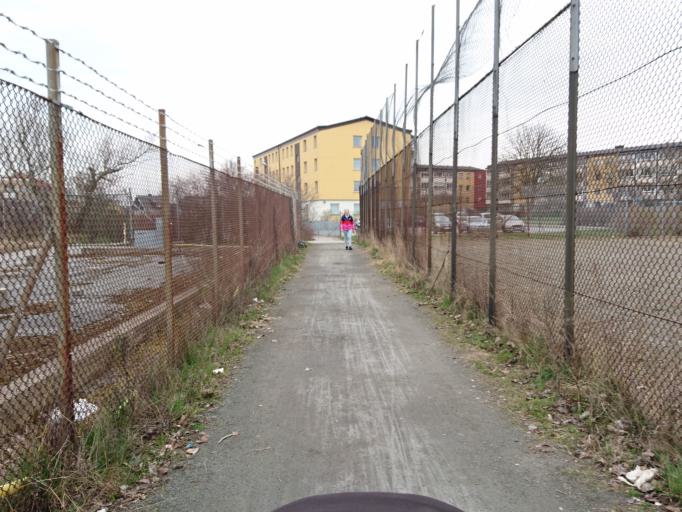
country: SE
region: Skane
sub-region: Malmo
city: Malmoe
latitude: 55.5784
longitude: 13.0308
